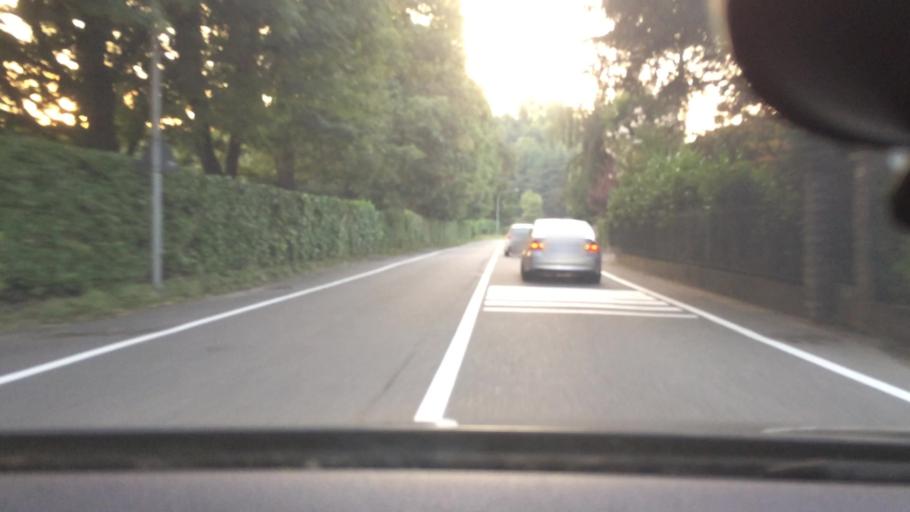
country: IT
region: Lombardy
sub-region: Provincia di Como
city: Anzano del Parco
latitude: 45.7719
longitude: 9.1949
